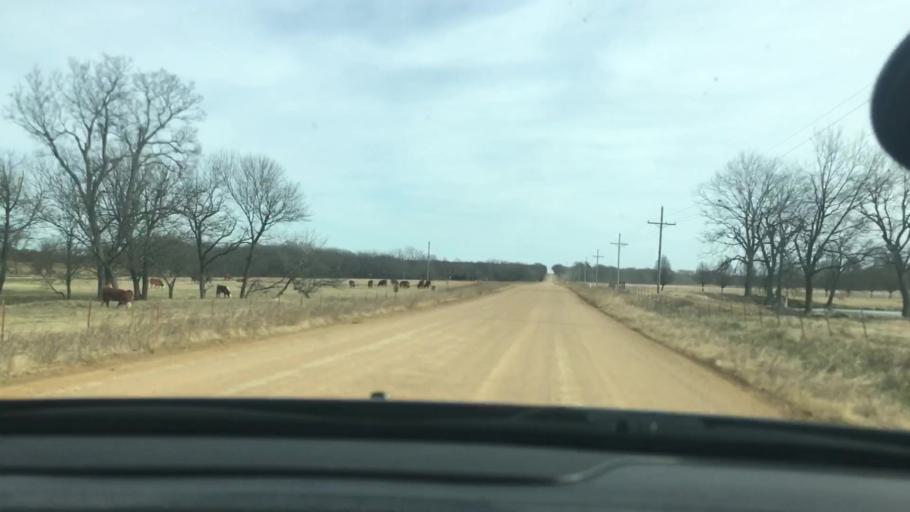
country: US
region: Oklahoma
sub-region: Murray County
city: Sulphur
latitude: 34.4051
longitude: -96.9127
